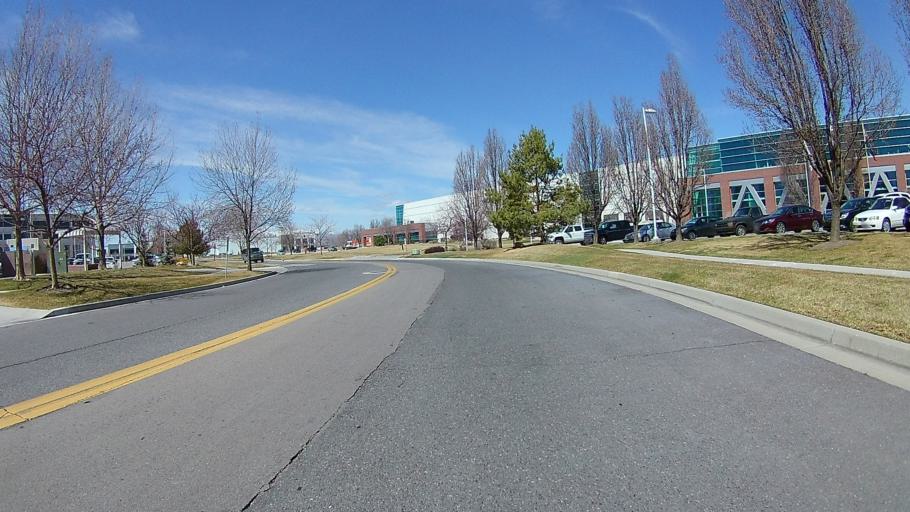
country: US
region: Utah
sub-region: Utah County
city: American Fork
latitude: 40.3534
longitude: -111.7777
